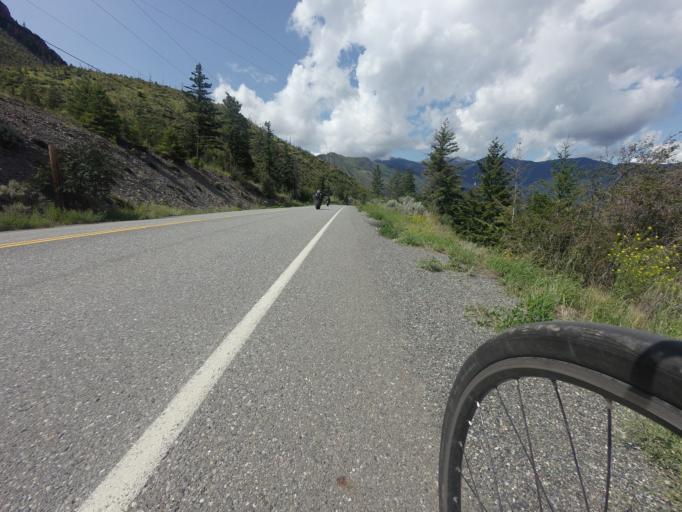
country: CA
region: British Columbia
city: Lillooet
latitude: 50.7575
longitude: -121.9158
